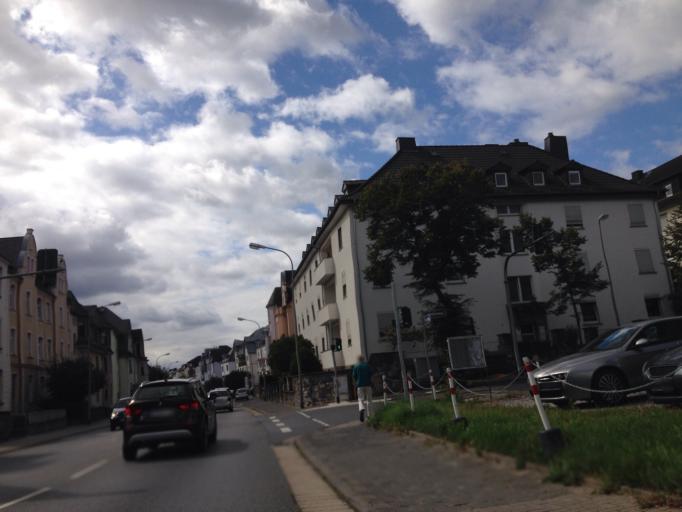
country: DE
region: Hesse
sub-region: Regierungsbezirk Giessen
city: Limburg an der Lahn
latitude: 50.3836
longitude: 8.0516
